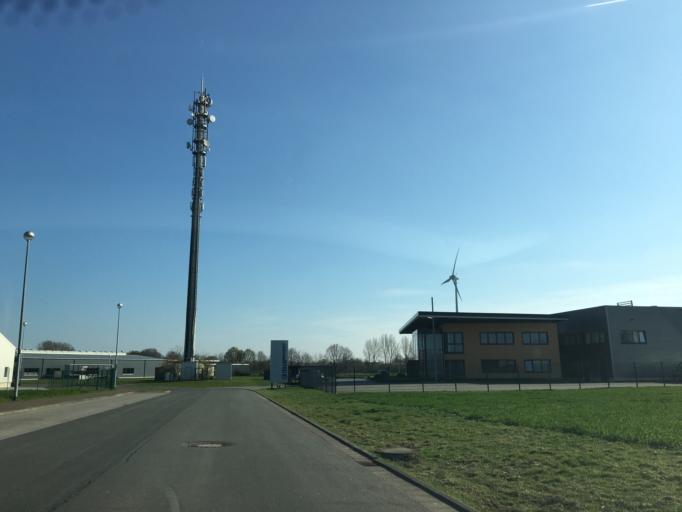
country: DE
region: North Rhine-Westphalia
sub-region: Regierungsbezirk Munster
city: Greven
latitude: 52.1119
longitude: 7.6207
